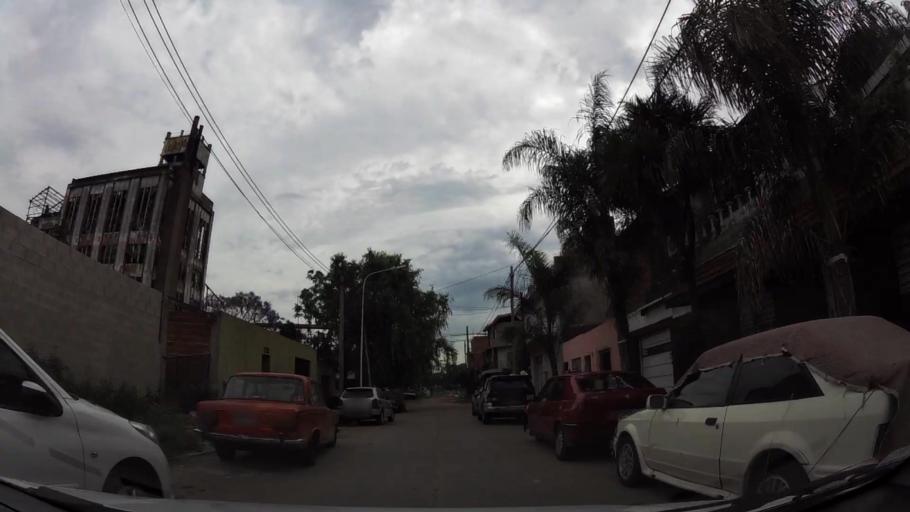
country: AR
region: Buenos Aires F.D.
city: Villa Lugano
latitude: -34.6778
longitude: -58.5027
